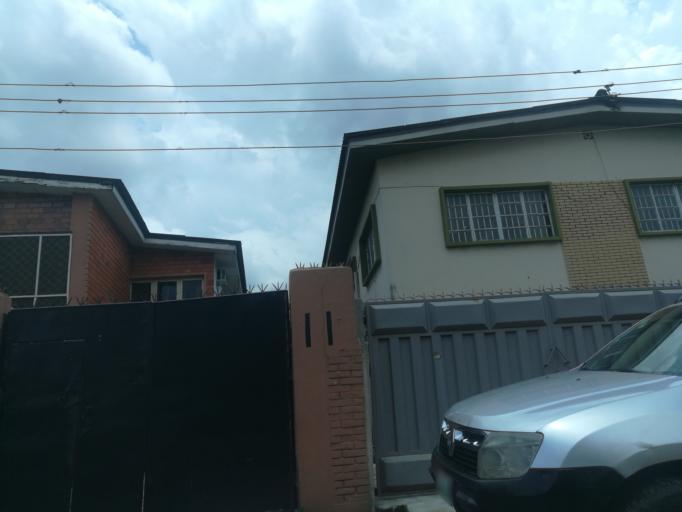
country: NG
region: Lagos
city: Somolu
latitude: 6.5486
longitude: 3.3587
